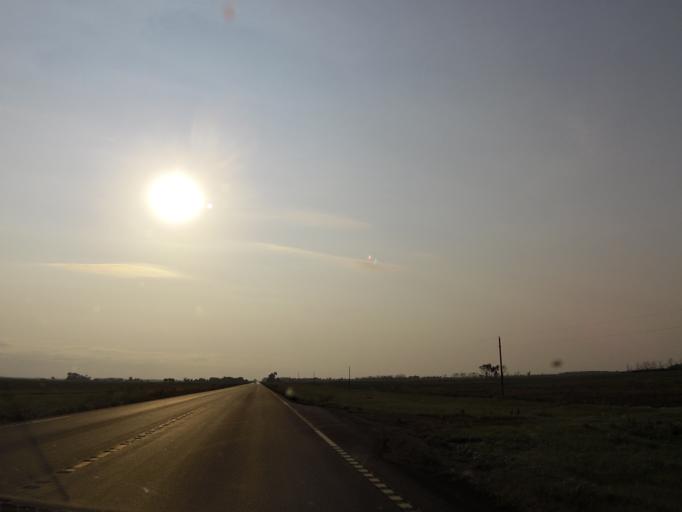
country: US
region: North Dakota
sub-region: Traill County
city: Mayville
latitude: 47.3529
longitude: -97.2661
